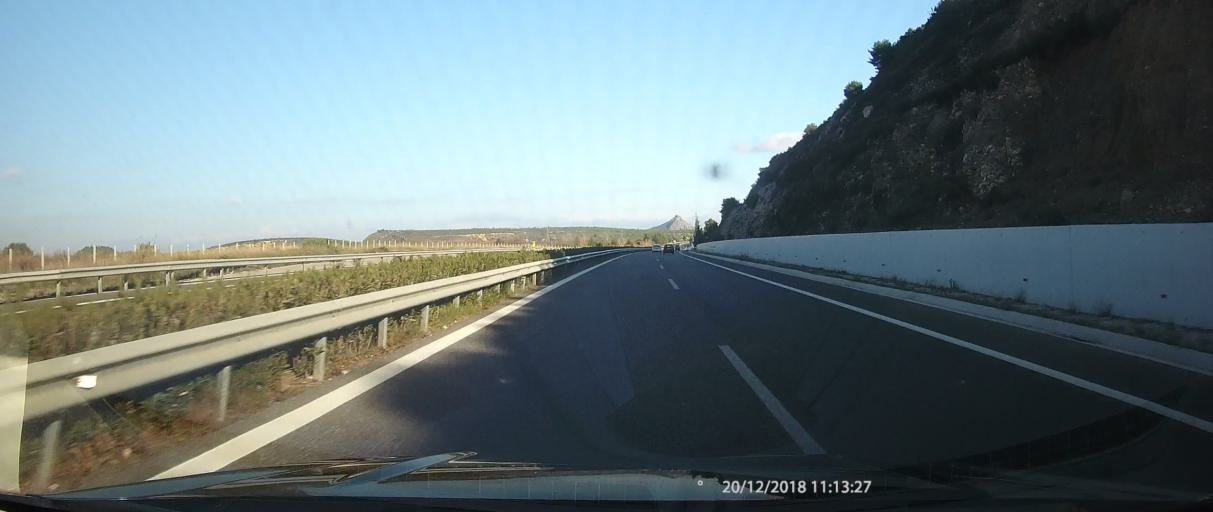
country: GR
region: Peloponnese
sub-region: Nomos Korinthias
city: Khiliomodhi
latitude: 37.8531
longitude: 22.8309
